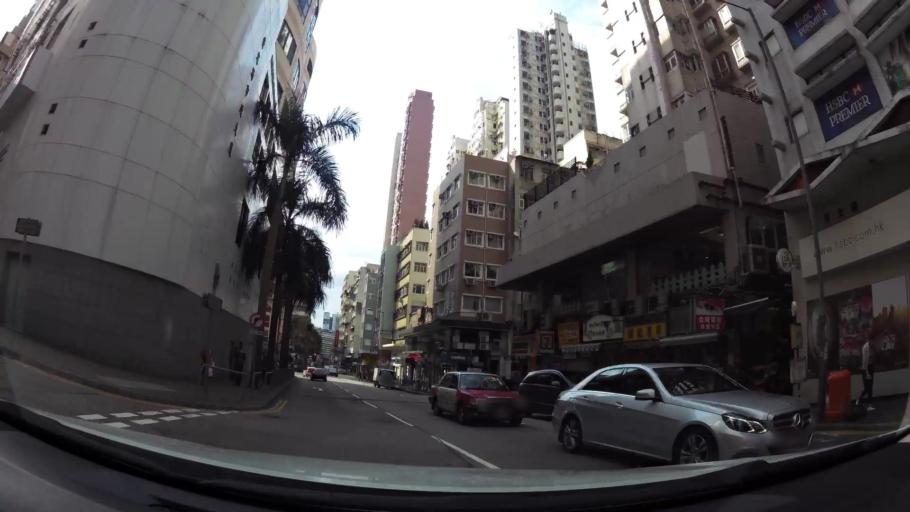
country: HK
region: Wanchai
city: Wan Chai
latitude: 22.2691
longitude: 114.1859
